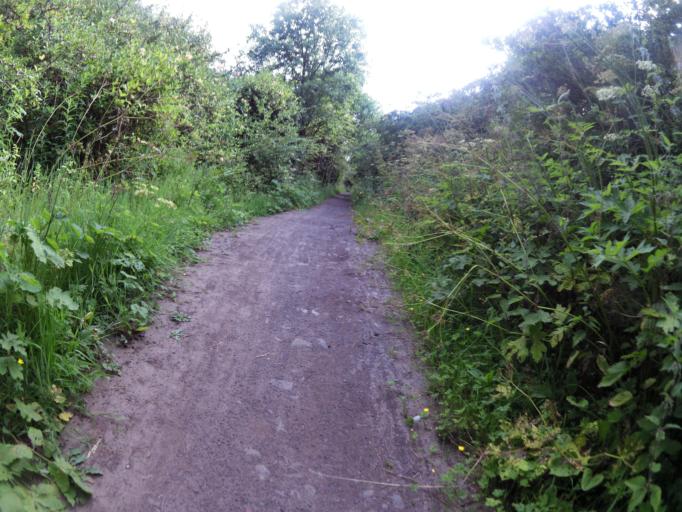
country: GB
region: Scotland
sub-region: Edinburgh
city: Queensferry
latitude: 55.9701
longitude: -3.3748
